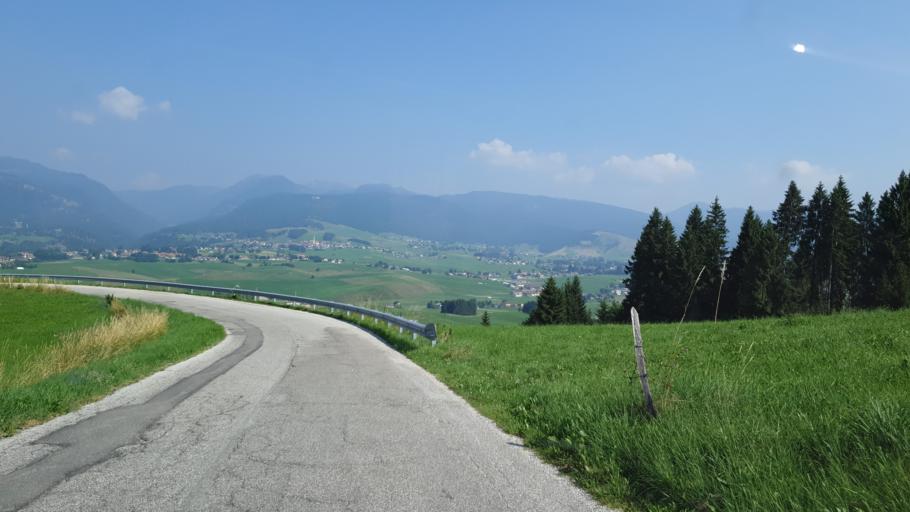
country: IT
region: Veneto
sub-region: Provincia di Vicenza
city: Canove di Roana
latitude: 45.8469
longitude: 11.4950
